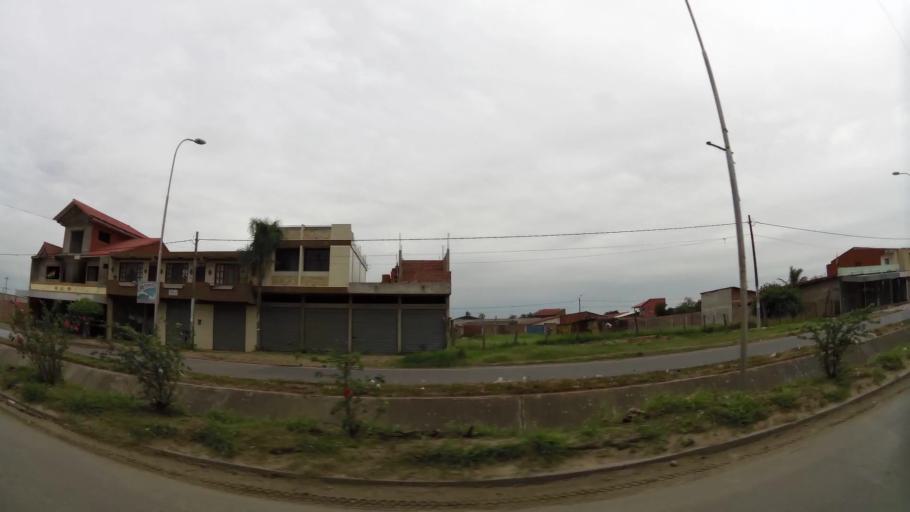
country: BO
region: Santa Cruz
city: Santa Cruz de la Sierra
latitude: -17.8465
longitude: -63.1688
